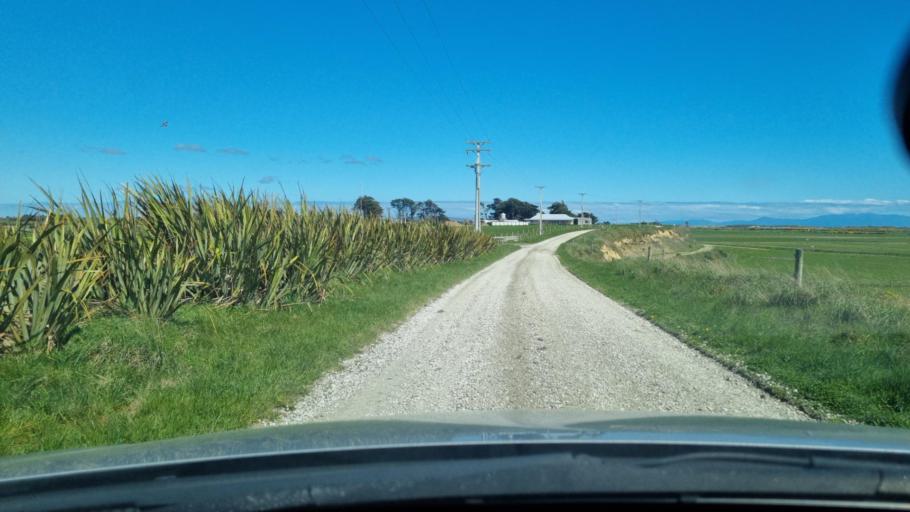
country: NZ
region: Southland
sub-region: Invercargill City
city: Invercargill
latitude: -46.3969
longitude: 168.2577
